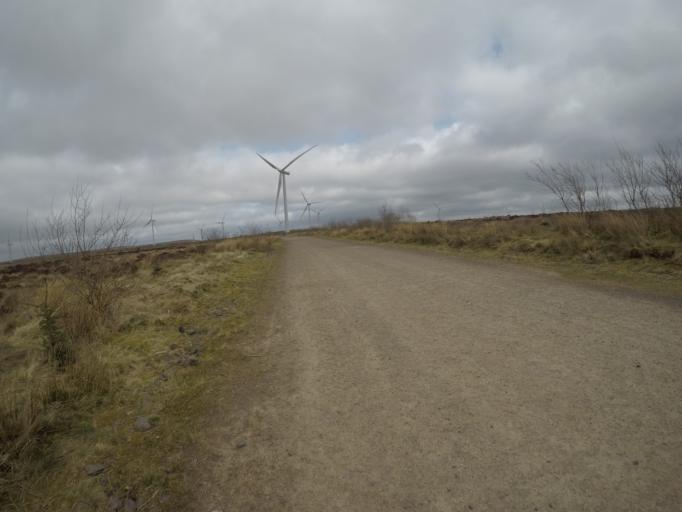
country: GB
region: Scotland
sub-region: East Renfrewshire
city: Newton Mearns
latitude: 55.6983
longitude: -4.3436
